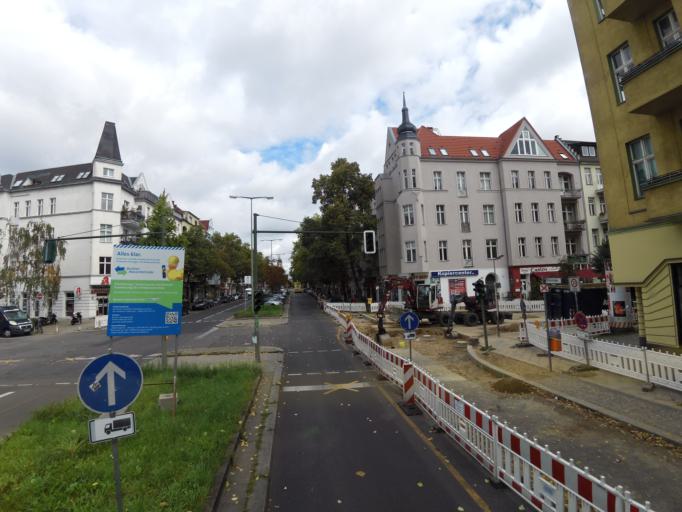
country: DE
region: Berlin
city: Friedenau
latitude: 52.4672
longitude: 13.3308
